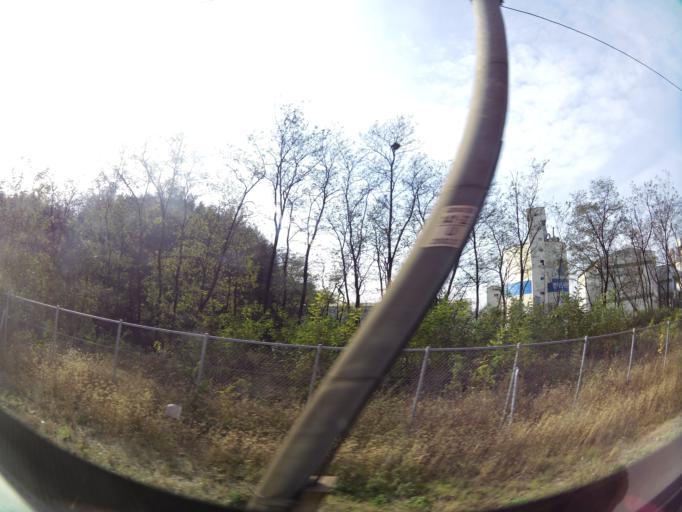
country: KR
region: Daejeon
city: Sintansin
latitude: 36.5215
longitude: 127.3747
